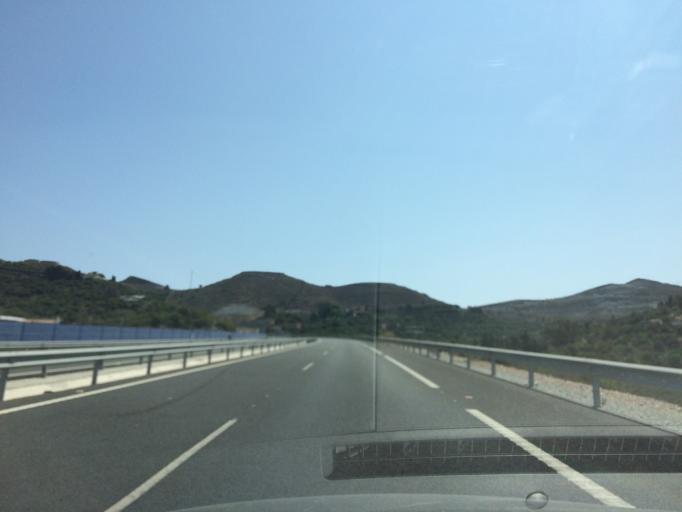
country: ES
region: Andalusia
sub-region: Provincia de Granada
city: El Varadero
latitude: 36.7207
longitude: -3.4637
